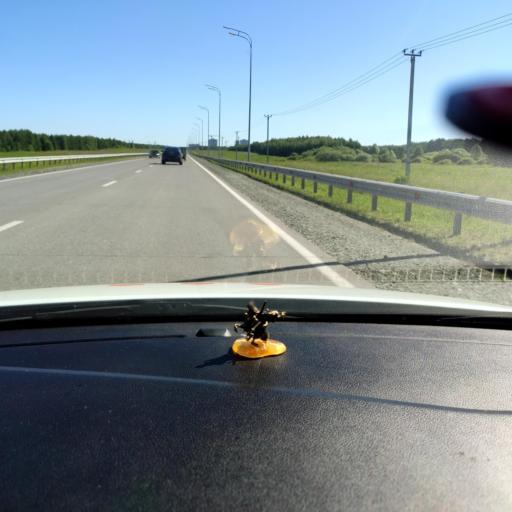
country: RU
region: Tatarstan
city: Stolbishchi
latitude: 55.6677
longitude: 49.1678
